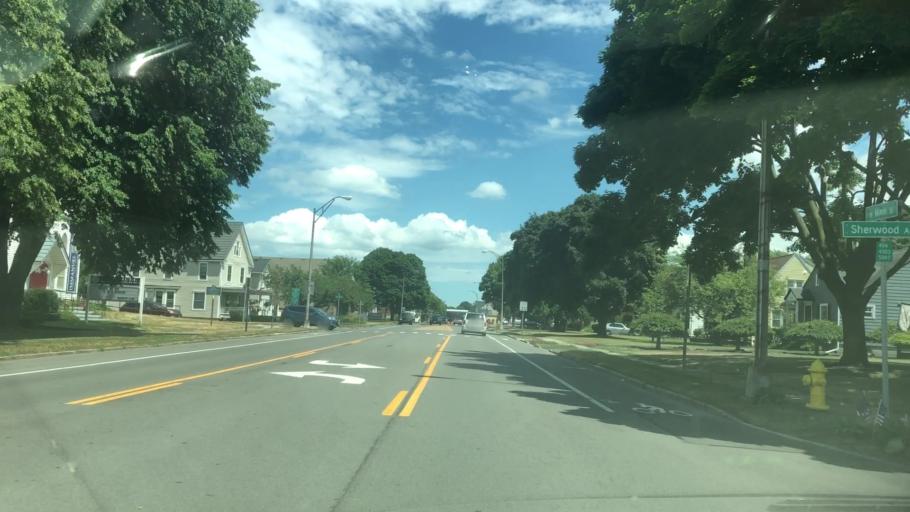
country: US
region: New York
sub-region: Monroe County
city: Webster
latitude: 43.2115
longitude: -77.4360
